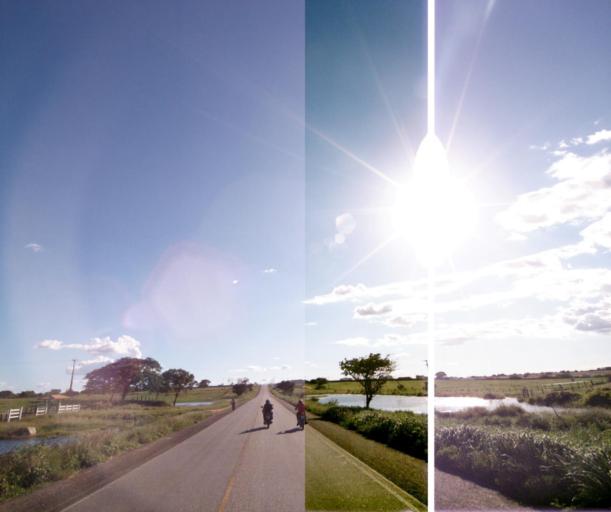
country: BR
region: Bahia
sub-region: Guanambi
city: Guanambi
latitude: -14.1948
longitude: -42.7483
